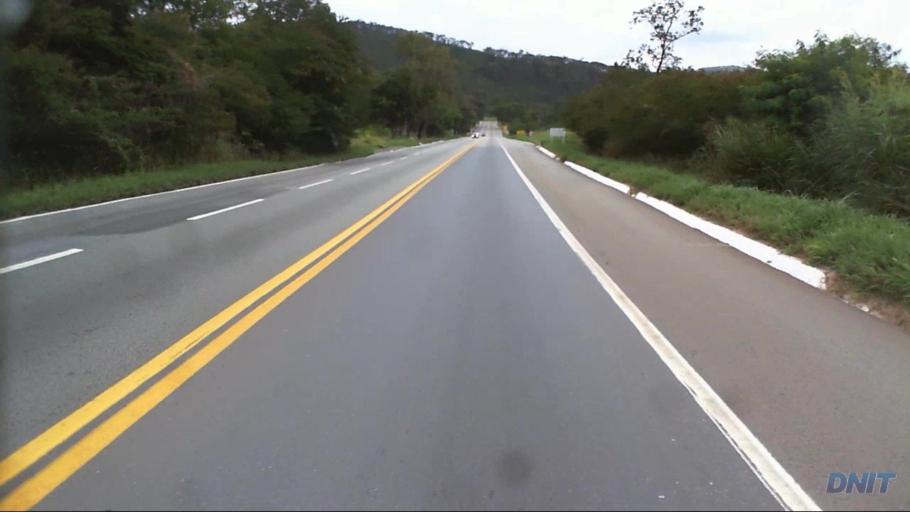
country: BR
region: Minas Gerais
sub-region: Caete
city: Caete
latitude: -19.7866
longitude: -43.7255
